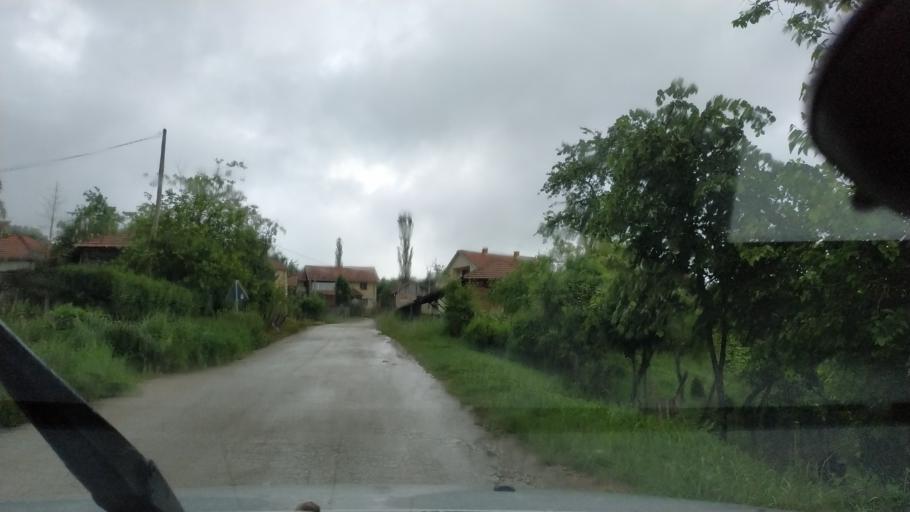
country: RS
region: Central Serbia
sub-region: Toplicki Okrug
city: Prokuplje
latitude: 43.3990
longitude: 21.5539
